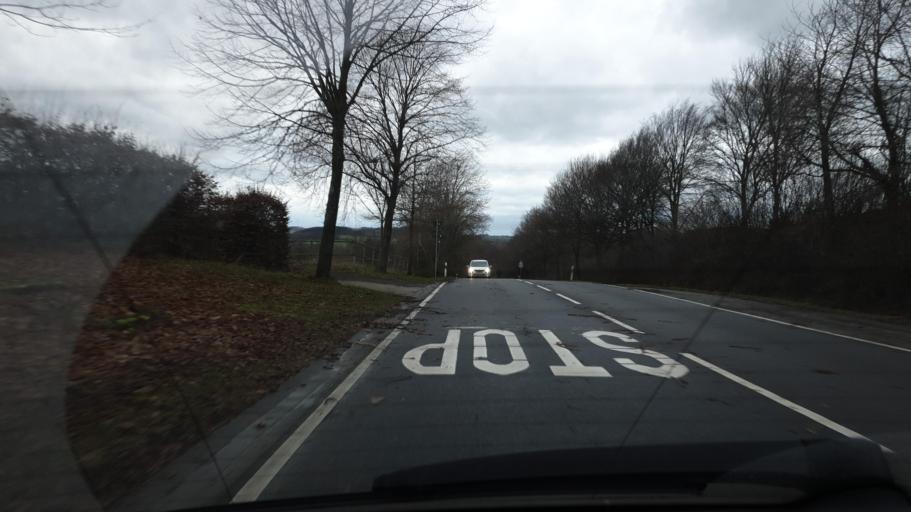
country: DE
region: North Rhine-Westphalia
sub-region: Regierungsbezirk Detmold
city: Vlotho
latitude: 52.1264
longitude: 8.8515
